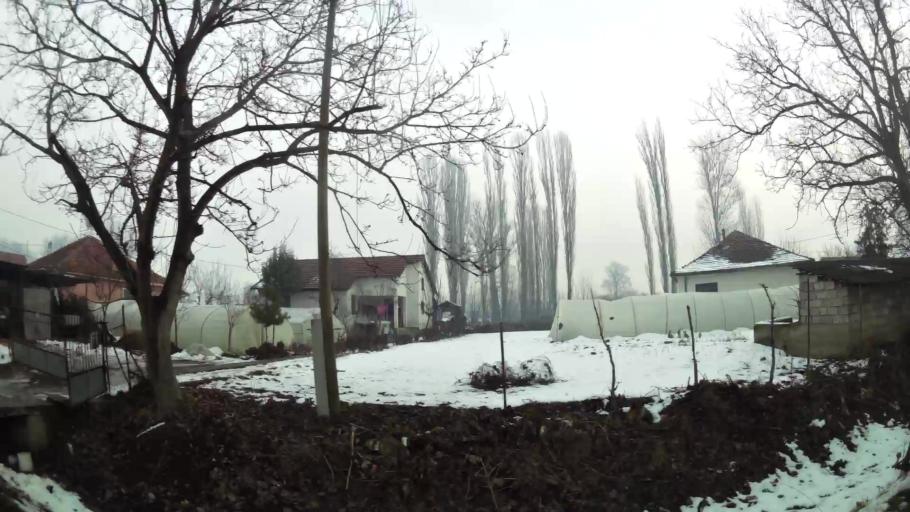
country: MK
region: Ilinden
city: Idrizovo
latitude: 41.9644
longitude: 21.5719
